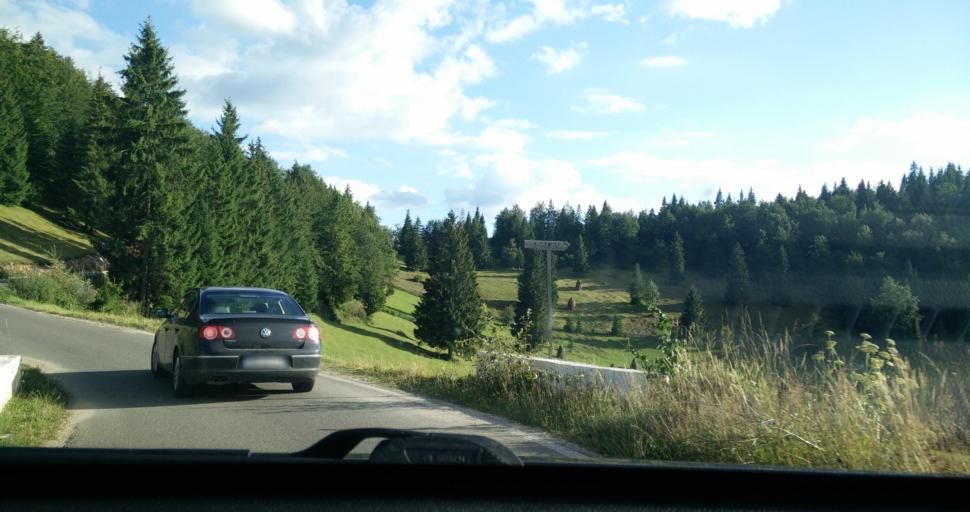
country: RO
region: Alba
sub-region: Comuna Scarisoara
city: Scarisoara
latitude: 46.4800
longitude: 22.8302
